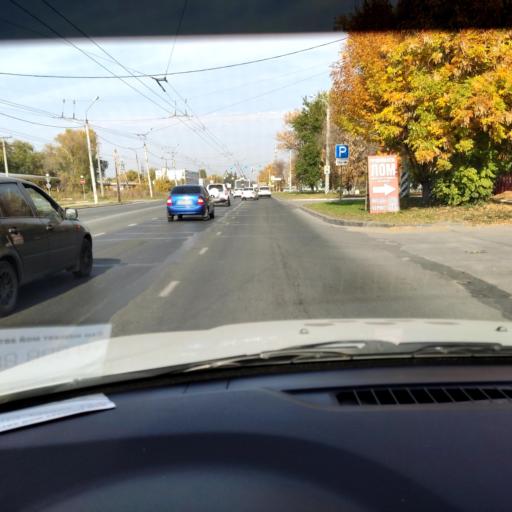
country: RU
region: Samara
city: Tol'yatti
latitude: 53.5336
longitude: 49.4397
